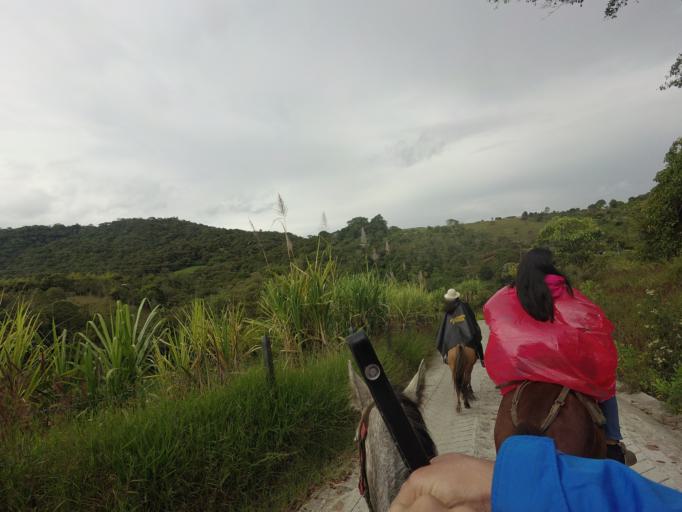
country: CO
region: Huila
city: San Agustin
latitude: 1.9075
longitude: -76.2943
